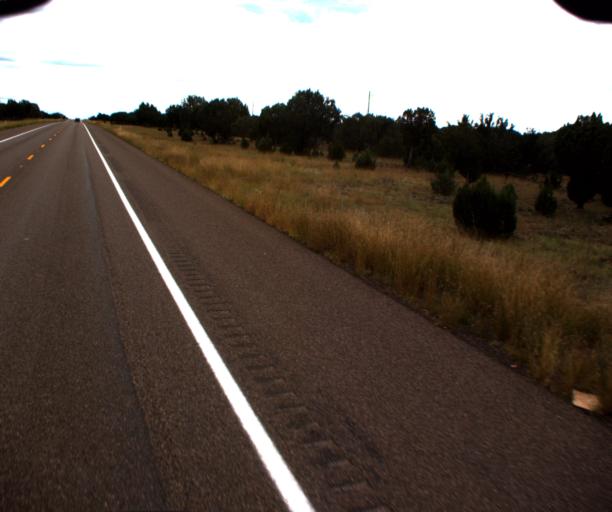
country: US
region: Arizona
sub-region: Navajo County
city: White Mountain Lake
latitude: 34.3134
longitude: -110.0401
